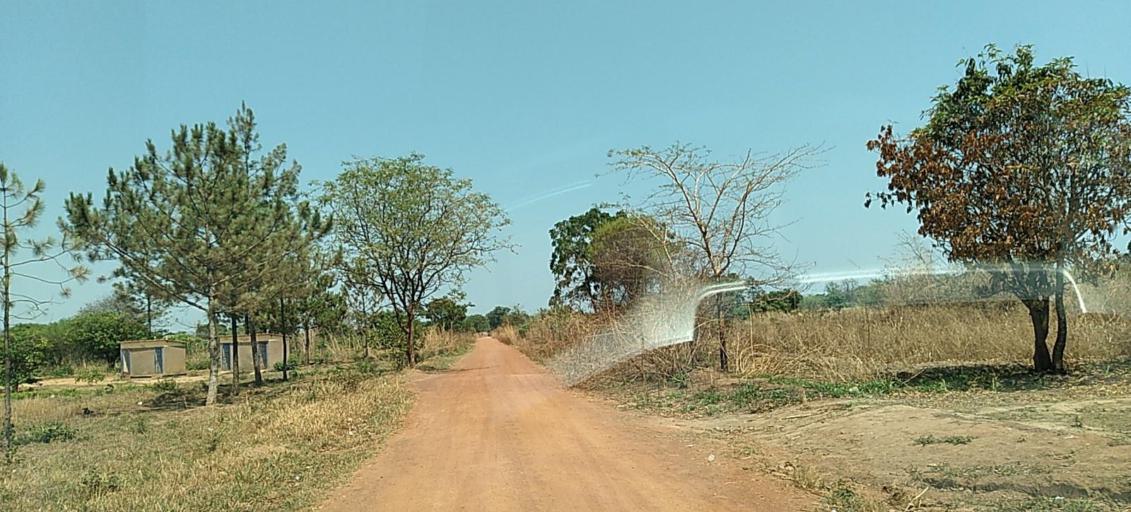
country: ZM
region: Copperbelt
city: Chingola
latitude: -12.5451
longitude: 27.7500
